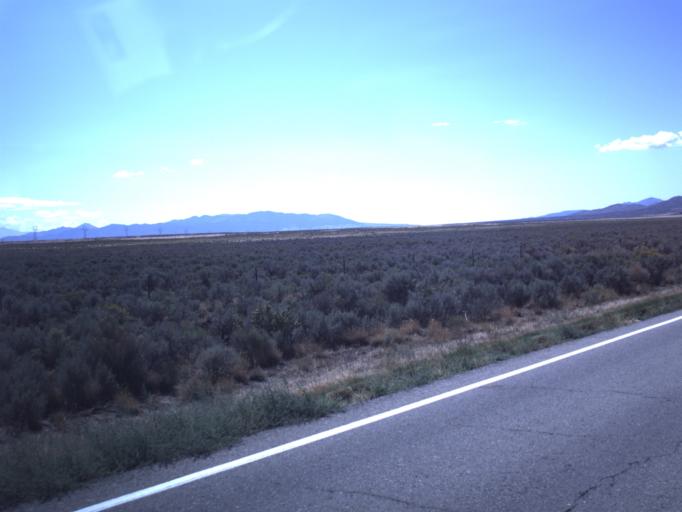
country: US
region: Utah
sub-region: Tooele County
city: Tooele
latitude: 40.2373
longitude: -112.4020
